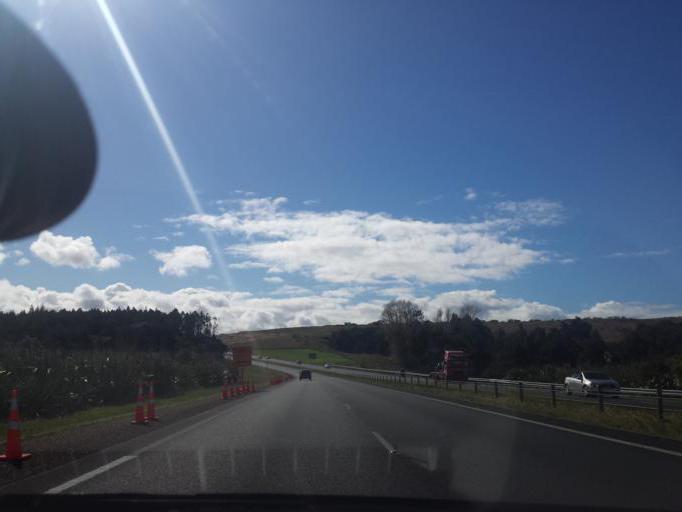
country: NZ
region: Auckland
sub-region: Auckland
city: Rothesay Bay
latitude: -36.6196
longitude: 174.6629
